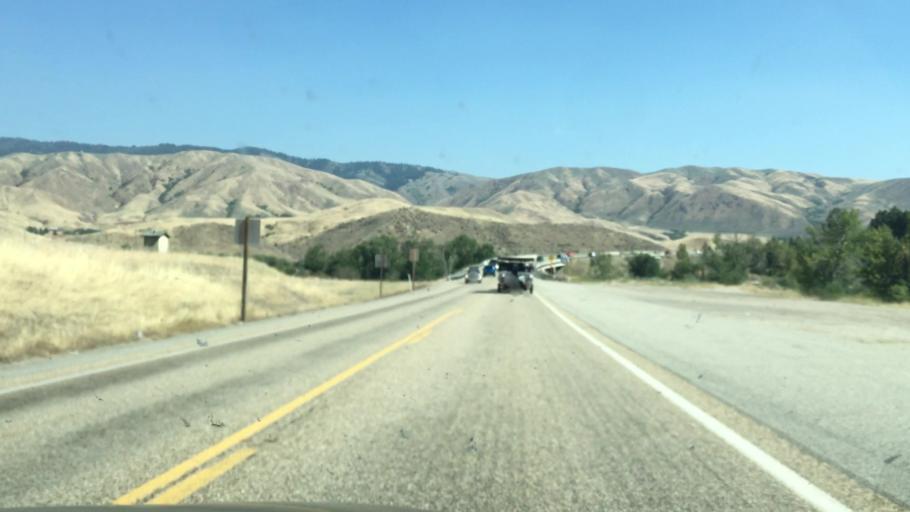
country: US
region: Idaho
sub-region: Ada County
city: Eagle
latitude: 43.9372
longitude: -116.1914
